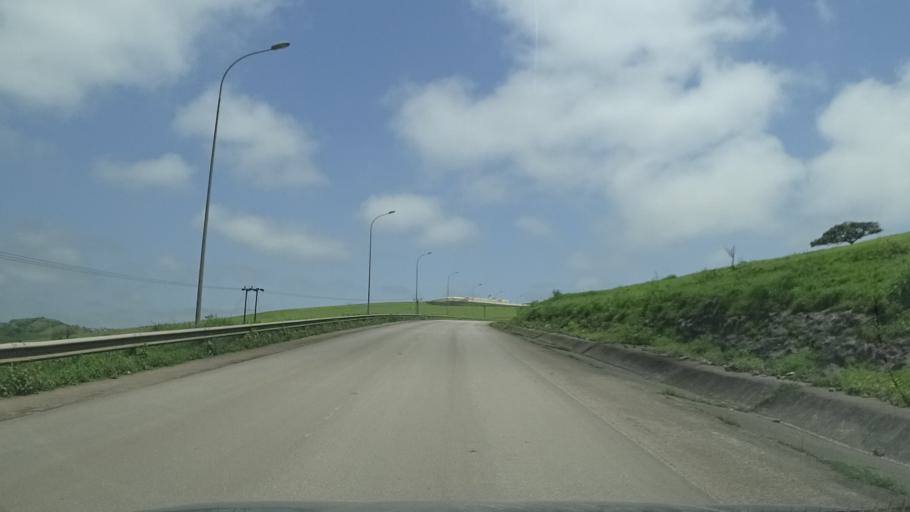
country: OM
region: Zufar
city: Salalah
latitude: 17.1849
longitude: 54.2509
